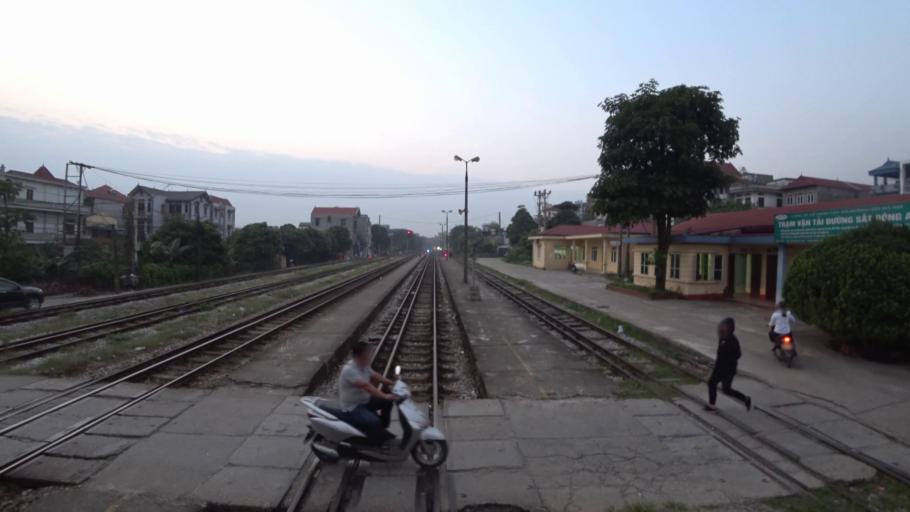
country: VN
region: Ha Noi
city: Soc Son
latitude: 21.2272
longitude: 105.8611
